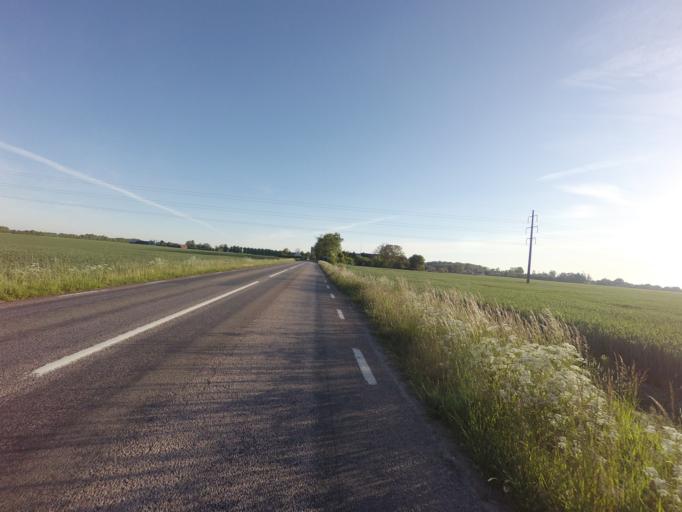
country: SE
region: Skane
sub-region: Helsingborg
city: Odakra
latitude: 56.1711
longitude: 12.6789
